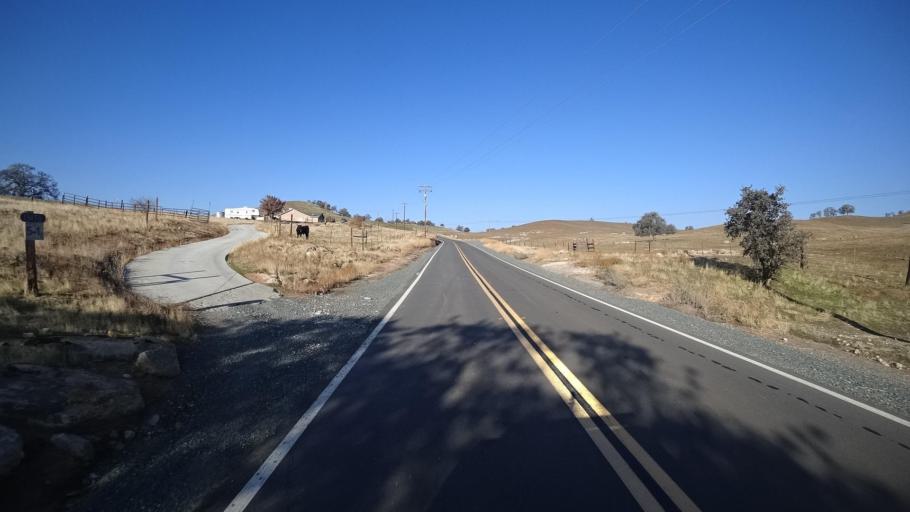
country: US
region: California
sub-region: Tulare County
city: Richgrove
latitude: 35.7102
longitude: -118.8401
